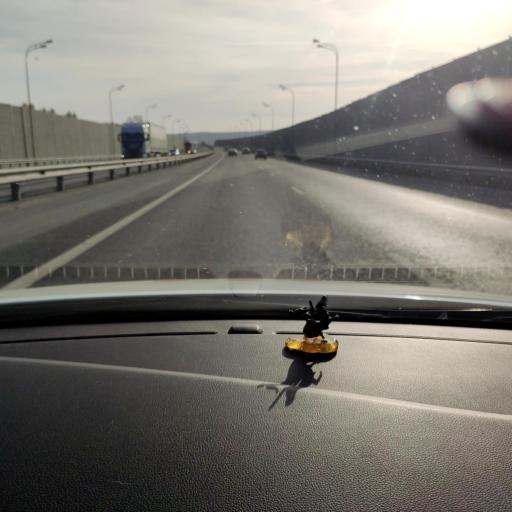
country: RU
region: Tatarstan
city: Osinovo
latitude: 55.8222
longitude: 48.8449
